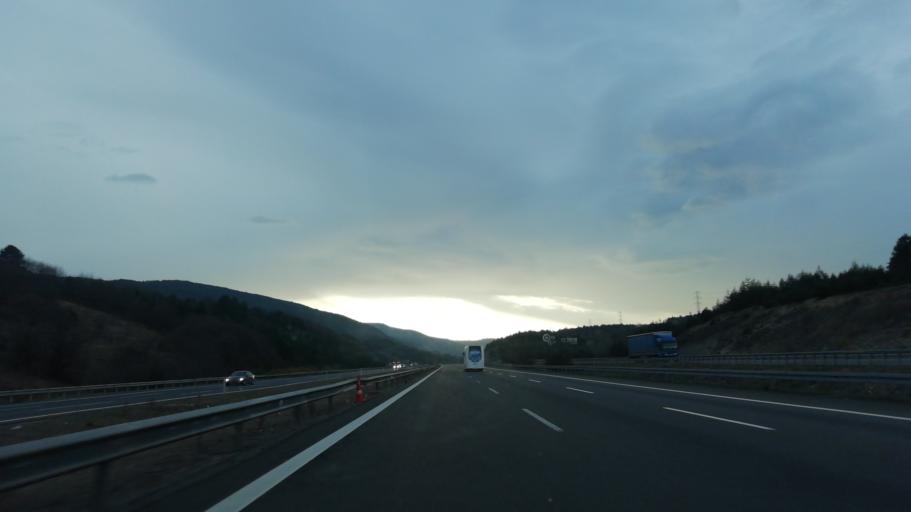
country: TR
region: Bolu
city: Yenicaga
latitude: 40.7530
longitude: 31.9082
